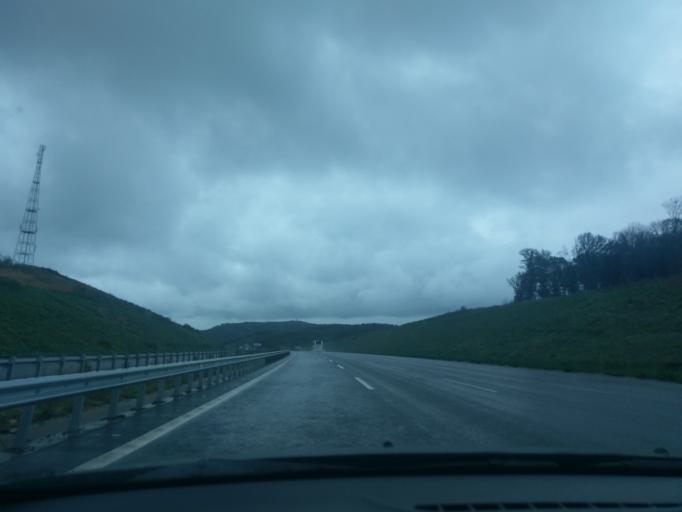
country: TR
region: Istanbul
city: Arikoey
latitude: 41.2308
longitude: 28.9325
